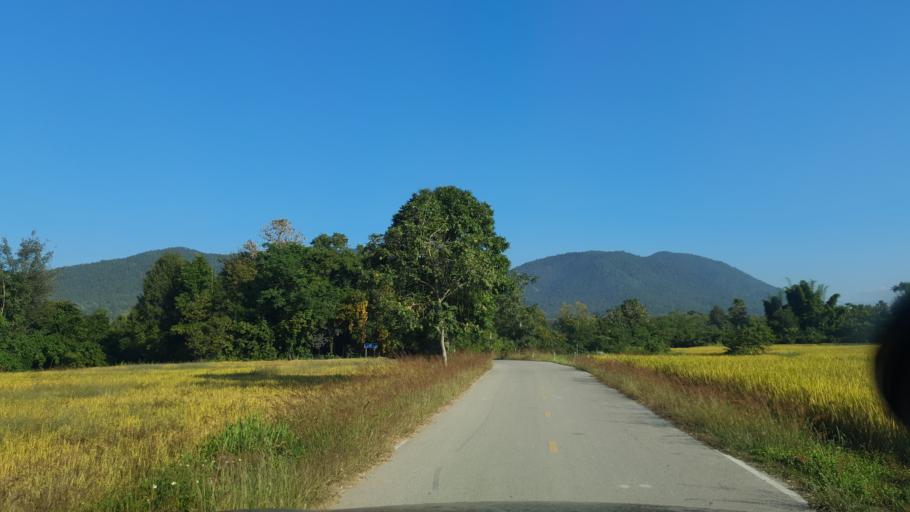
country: TH
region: Chiang Mai
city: Mae On
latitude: 18.7346
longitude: 99.2148
